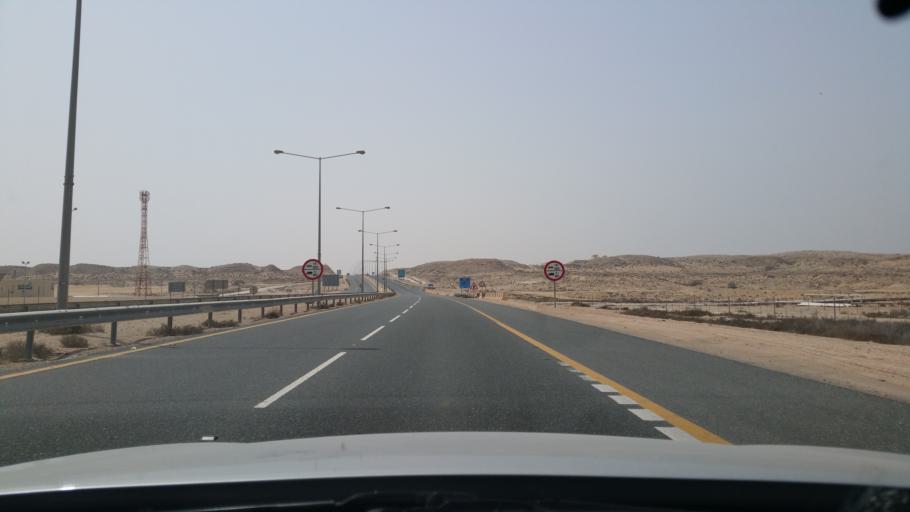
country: QA
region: Baladiyat ar Rayyan
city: Dukhan
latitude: 25.3354
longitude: 50.7835
